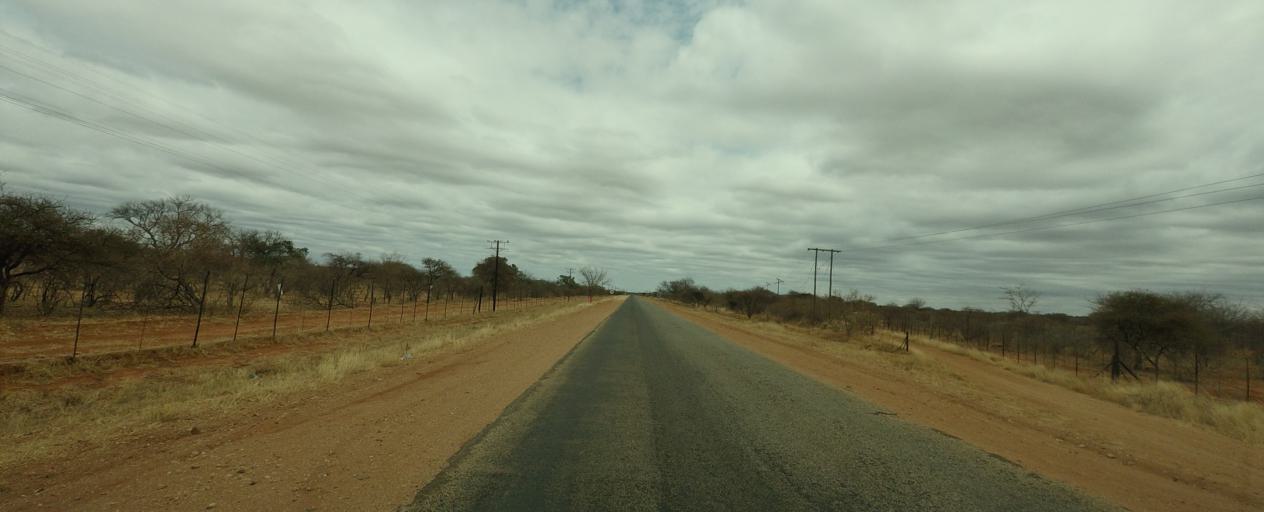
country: BW
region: Central
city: Mathathane
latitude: -22.6765
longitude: 29.0929
